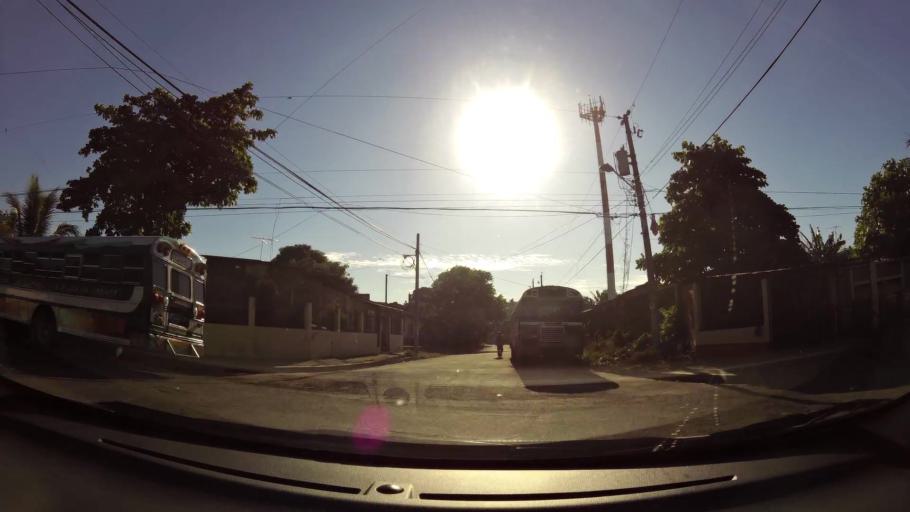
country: SV
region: Sonsonate
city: Sonsonate
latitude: 13.7142
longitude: -89.7161
